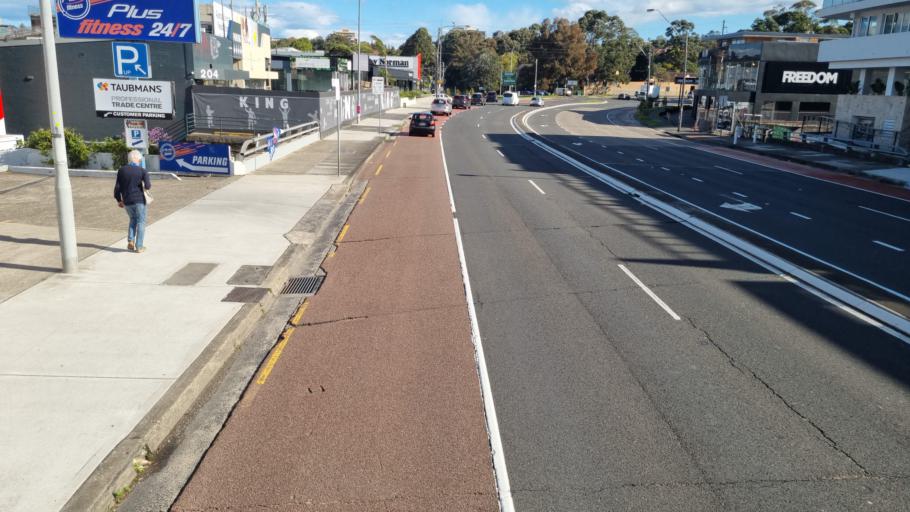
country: AU
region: New South Wales
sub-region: Manly Vale
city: Fairlight
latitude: -33.7871
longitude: 151.2666
